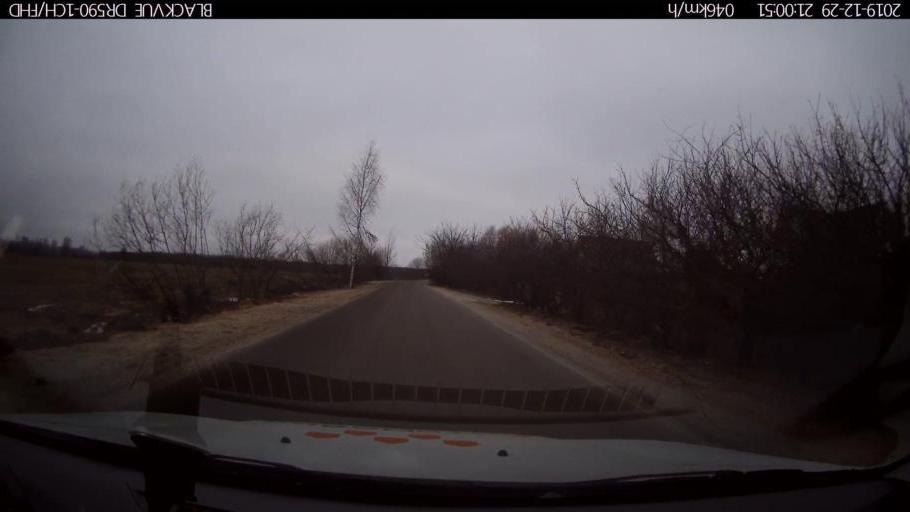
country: RU
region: Nizjnij Novgorod
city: Afonino
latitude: 56.1858
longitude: 43.9901
